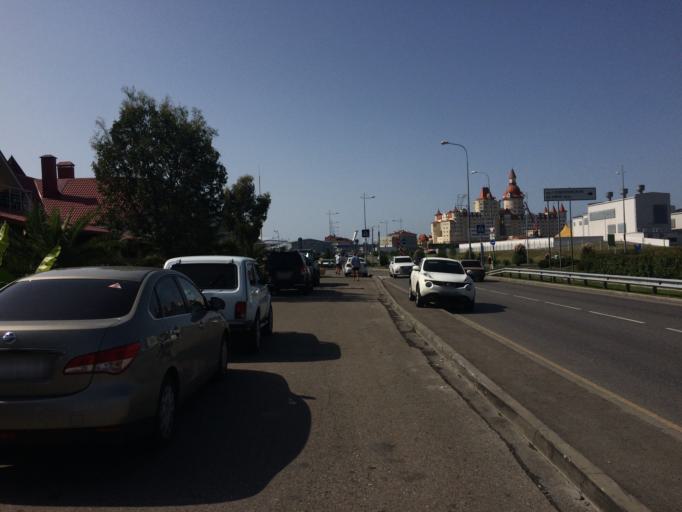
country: RU
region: Krasnodarskiy
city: Adler
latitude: 43.4005
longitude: 39.9691
